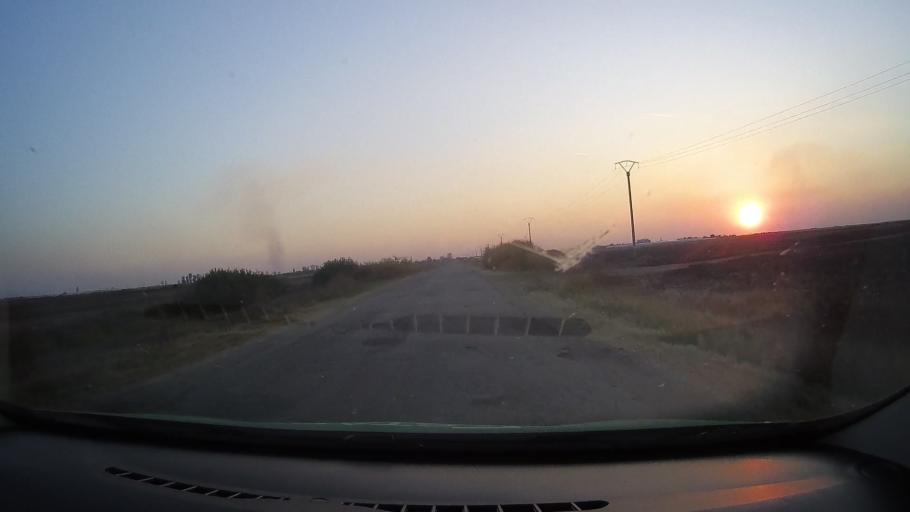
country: RO
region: Arad
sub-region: Comuna Olari
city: Olari
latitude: 46.3970
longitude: 21.5608
